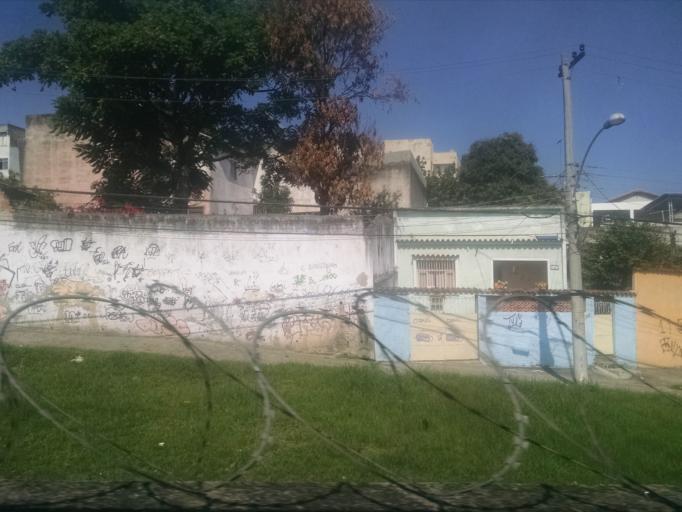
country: BR
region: Rio de Janeiro
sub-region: Sao Joao De Meriti
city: Sao Joao de Meriti
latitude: -22.8430
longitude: -43.3323
